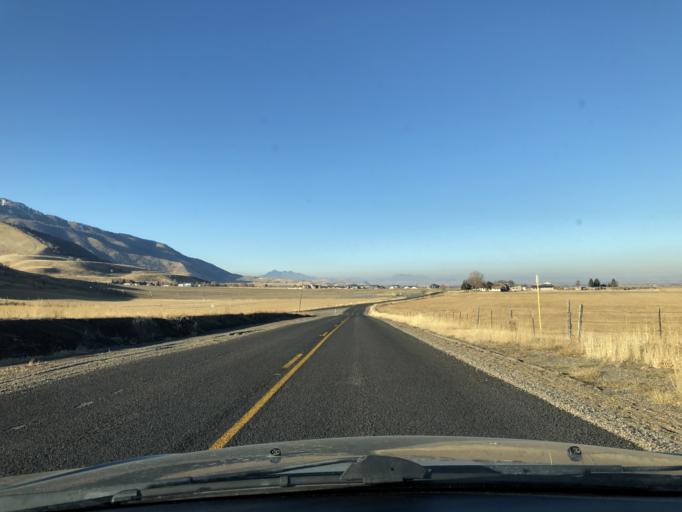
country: US
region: Utah
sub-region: Cache County
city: Wellsville
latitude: 41.5973
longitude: -111.9284
